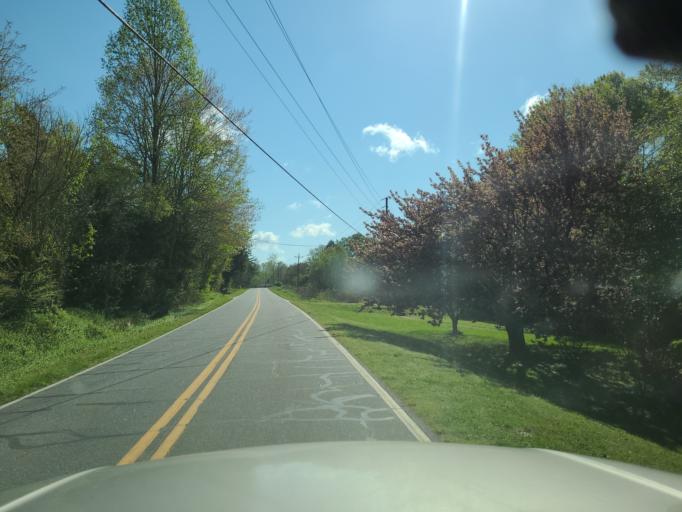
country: US
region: North Carolina
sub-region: Rutherford County
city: Spindale
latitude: 35.2957
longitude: -81.9551
